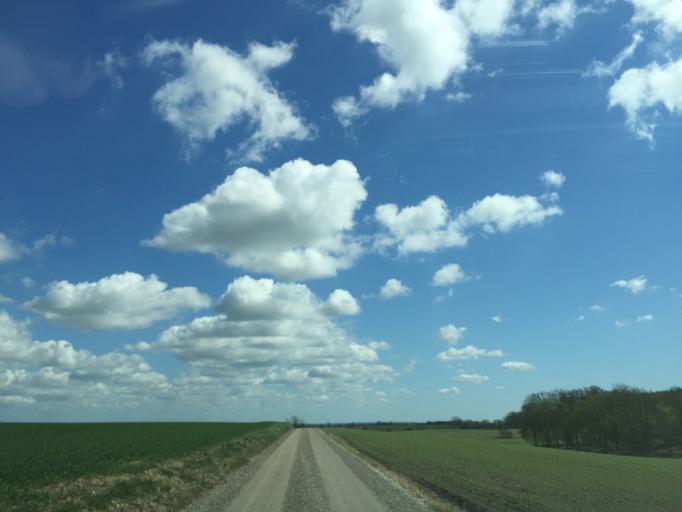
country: SE
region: Skane
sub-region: Lunds Kommun
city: Genarp
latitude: 55.7059
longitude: 13.3577
